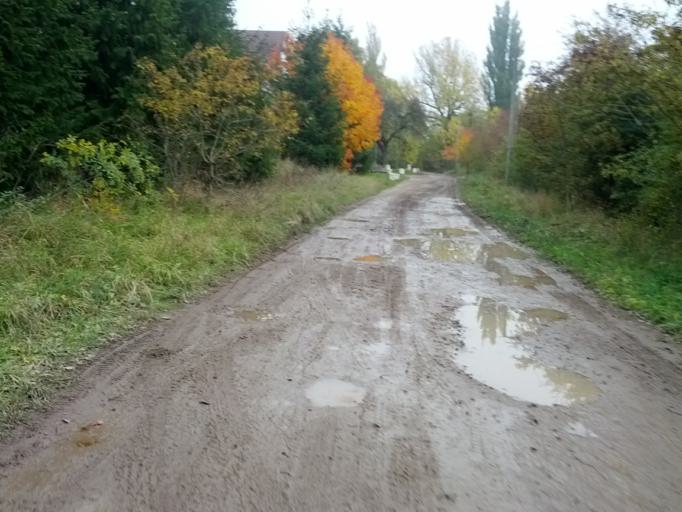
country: DE
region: Thuringia
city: Eisenach
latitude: 50.9930
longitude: 10.3697
